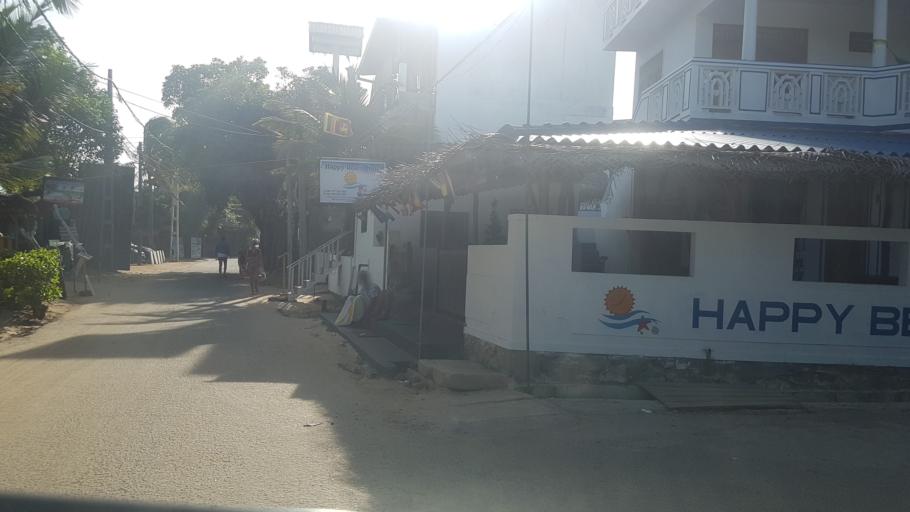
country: LK
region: Southern
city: Tangalla
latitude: 6.0333
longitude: 80.8008
